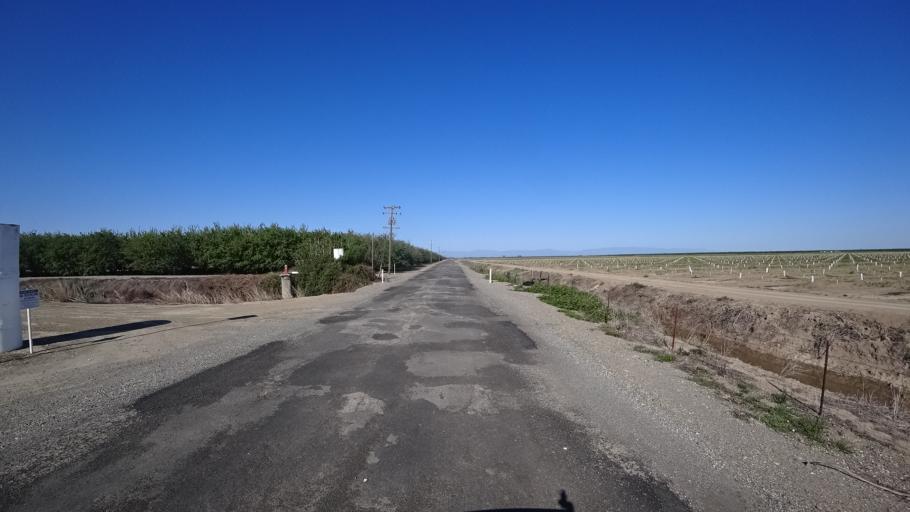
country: US
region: California
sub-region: Glenn County
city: Hamilton City
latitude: 39.6781
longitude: -122.0231
